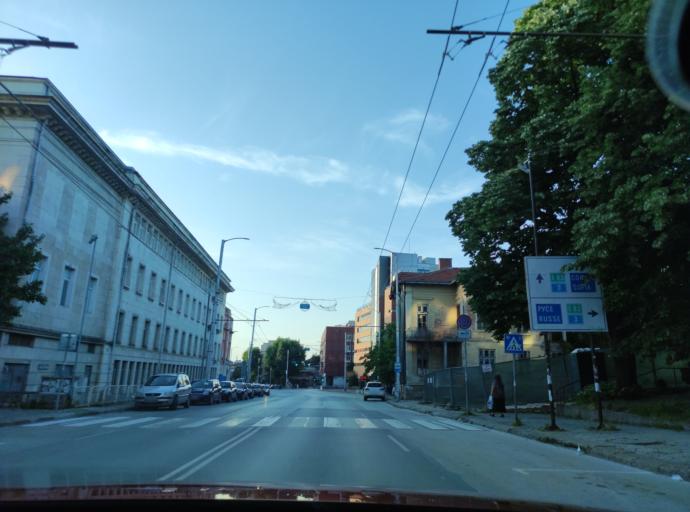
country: BG
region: Pleven
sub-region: Obshtina Pleven
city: Pleven
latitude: 43.4070
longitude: 24.6213
